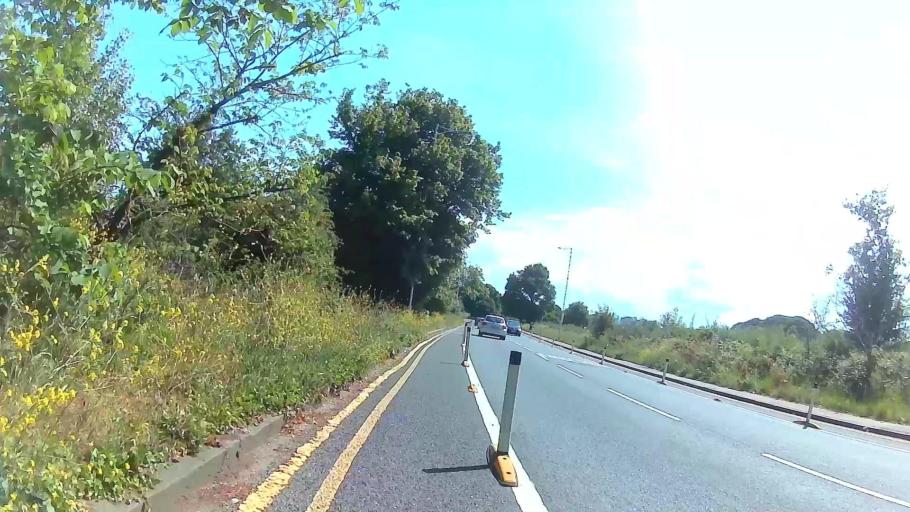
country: GB
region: England
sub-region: Greater London
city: East Ham
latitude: 51.5615
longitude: 0.0256
